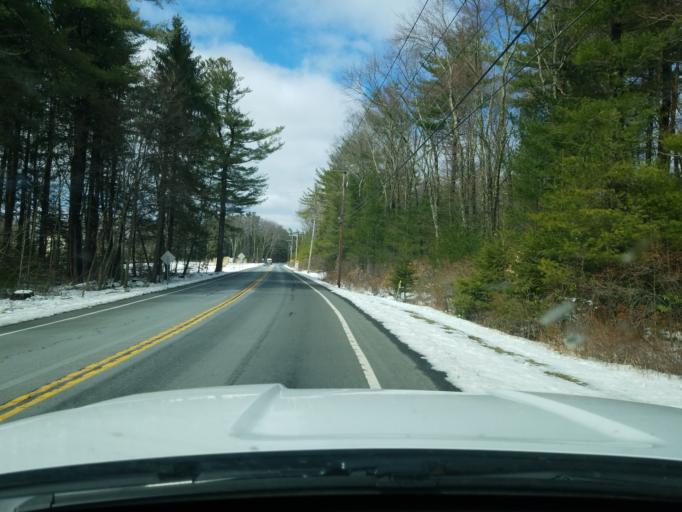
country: US
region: Connecticut
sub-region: Litchfield County
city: New Hartford Center
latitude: 41.8536
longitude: -72.9996
